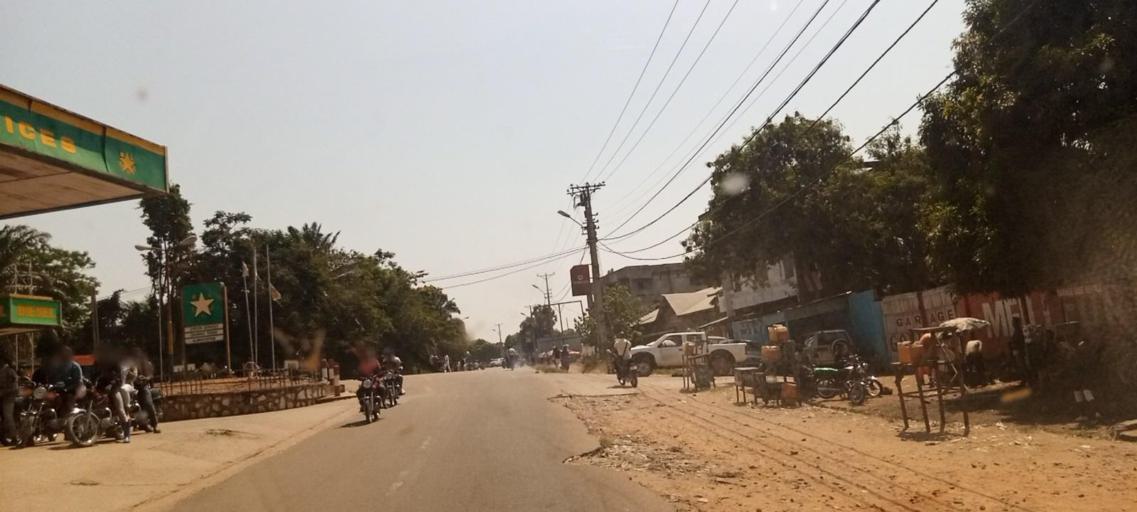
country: CD
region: Kasai-Oriental
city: Mbuji-Mayi
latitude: -6.1216
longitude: 23.5941
